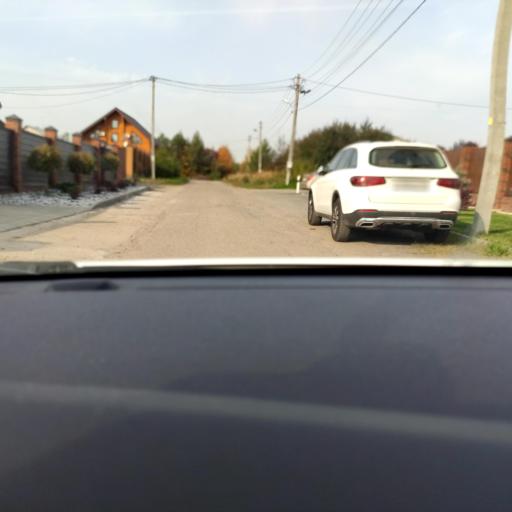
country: RU
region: Tatarstan
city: Vysokaya Gora
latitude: 55.8095
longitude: 49.2449
